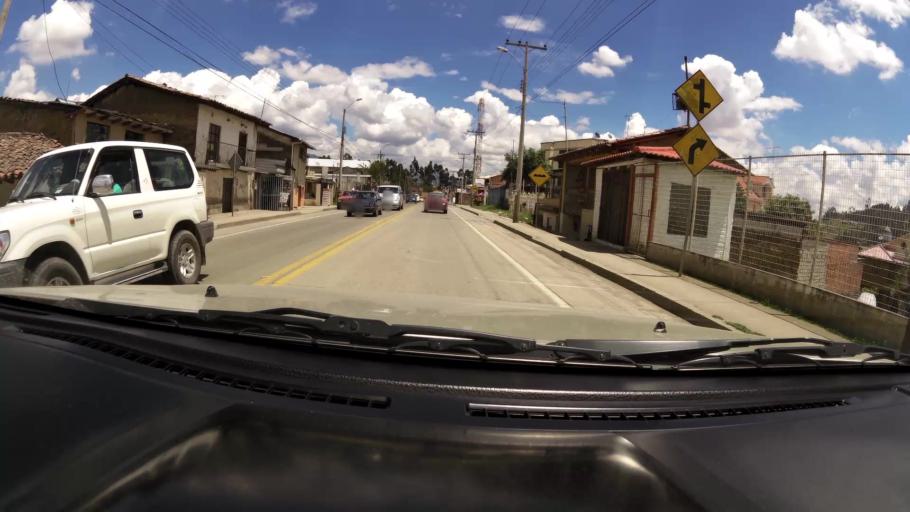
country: EC
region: Azuay
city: Cuenca
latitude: -2.9290
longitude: -79.0429
